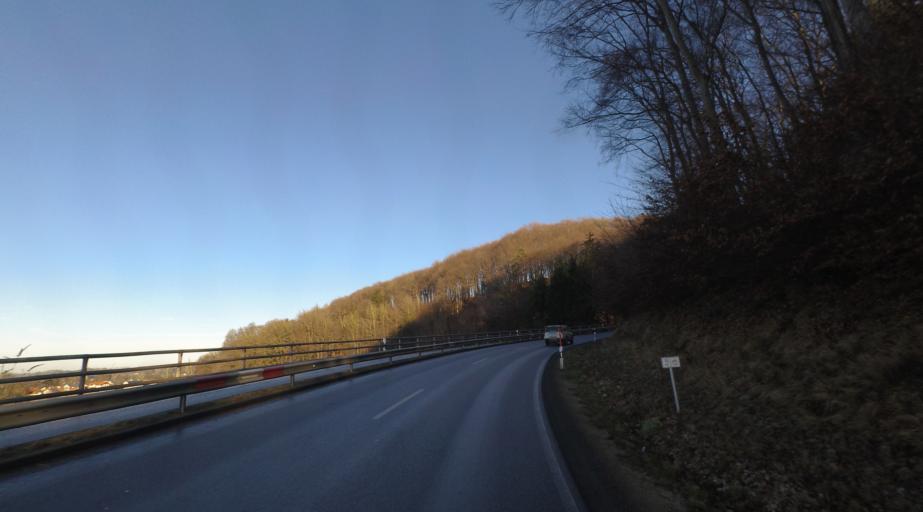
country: DE
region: Bavaria
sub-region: Upper Bavaria
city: Trostberg an der Alz
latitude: 48.0247
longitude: 12.5676
